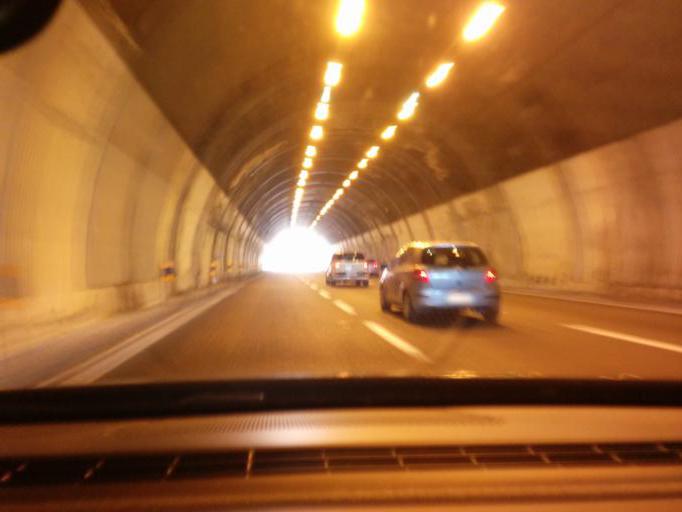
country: IT
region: Liguria
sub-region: Provincia di Genova
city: Arenzano
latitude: 44.4109
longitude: 8.6931
